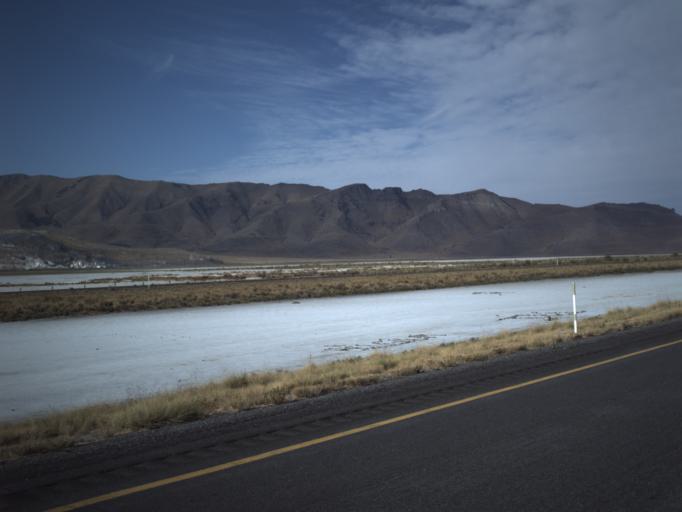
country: US
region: Utah
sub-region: Tooele County
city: Grantsville
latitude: 40.7136
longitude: -112.5382
